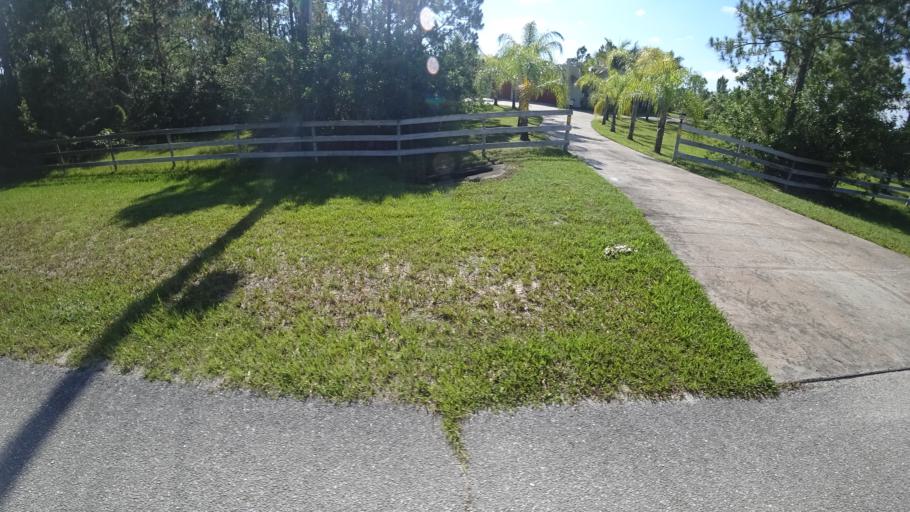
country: US
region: Florida
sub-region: Sarasota County
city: The Meadows
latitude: 27.4250
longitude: -82.3489
